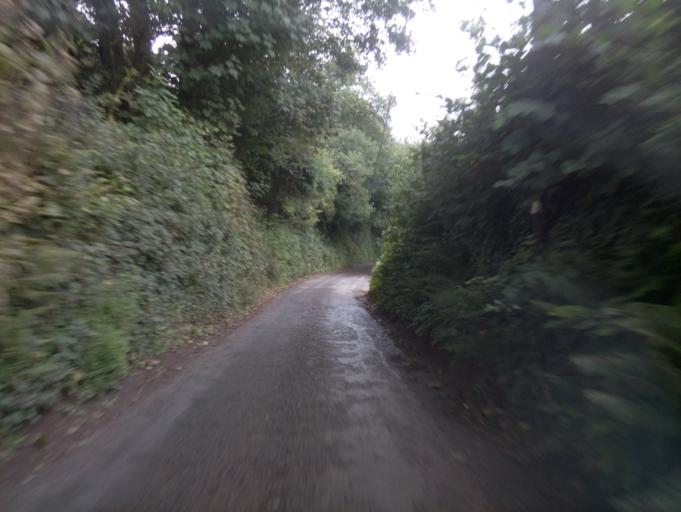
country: GB
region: England
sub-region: Devon
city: Kingsbridge
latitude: 50.2783
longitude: -3.7193
